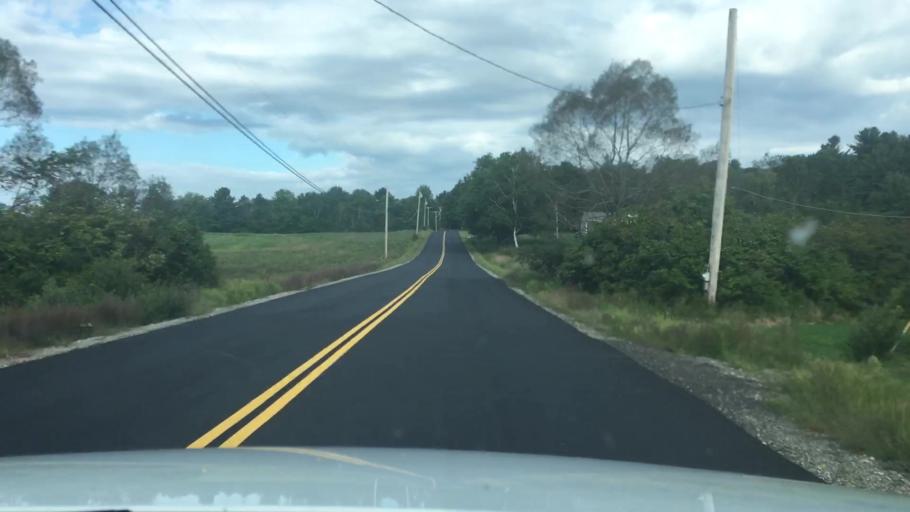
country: US
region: Maine
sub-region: Androscoggin County
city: Lisbon Falls
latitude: 44.0402
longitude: -70.0366
